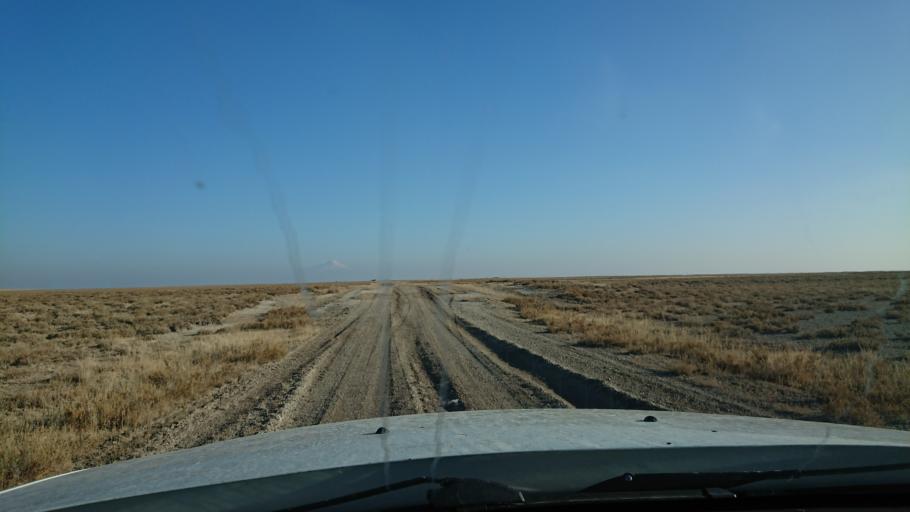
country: TR
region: Aksaray
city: Sultanhani
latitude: 38.4020
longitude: 33.5789
